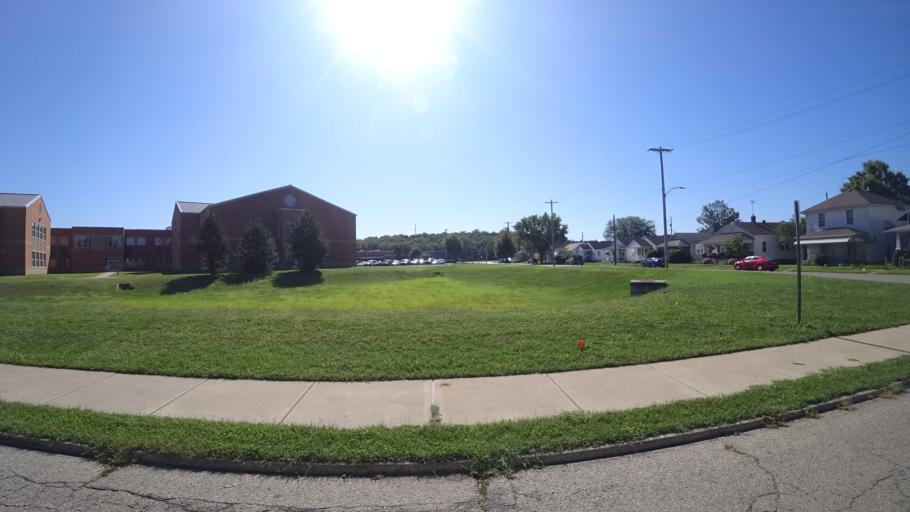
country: US
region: Ohio
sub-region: Butler County
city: Hamilton
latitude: 39.3966
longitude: -84.5437
